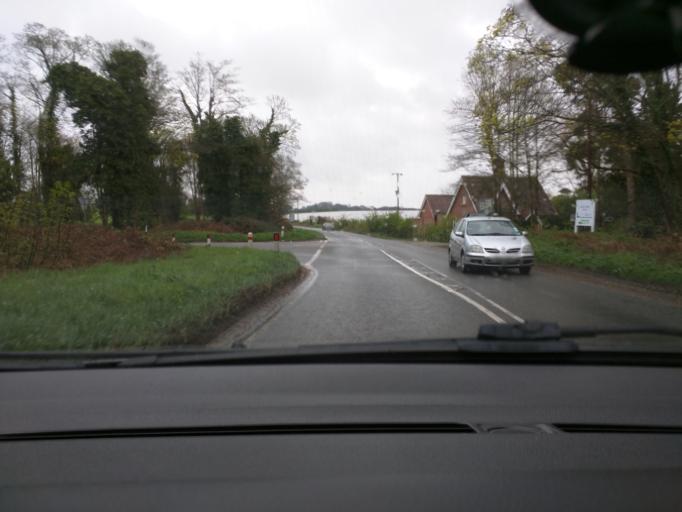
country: GB
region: England
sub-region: Suffolk
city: Leiston
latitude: 52.1790
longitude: 1.5374
